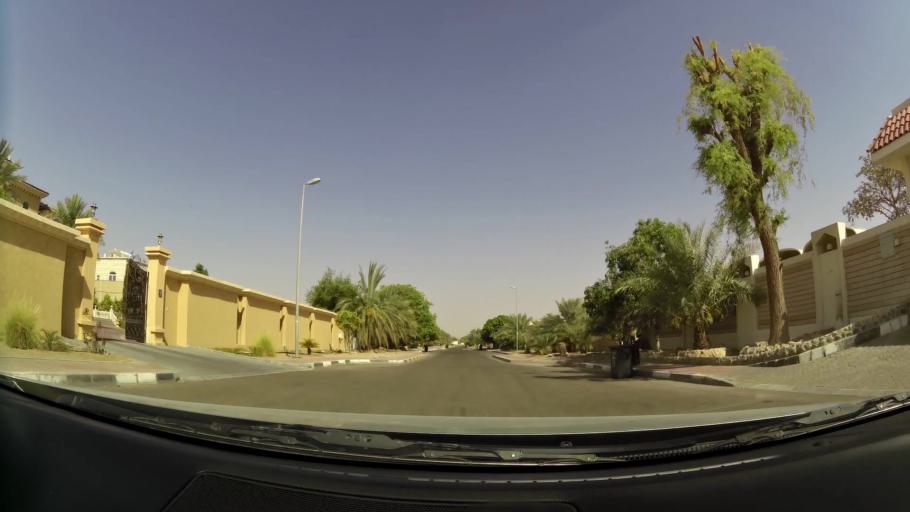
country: OM
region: Al Buraimi
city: Al Buraymi
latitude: 24.3116
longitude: 55.8063
